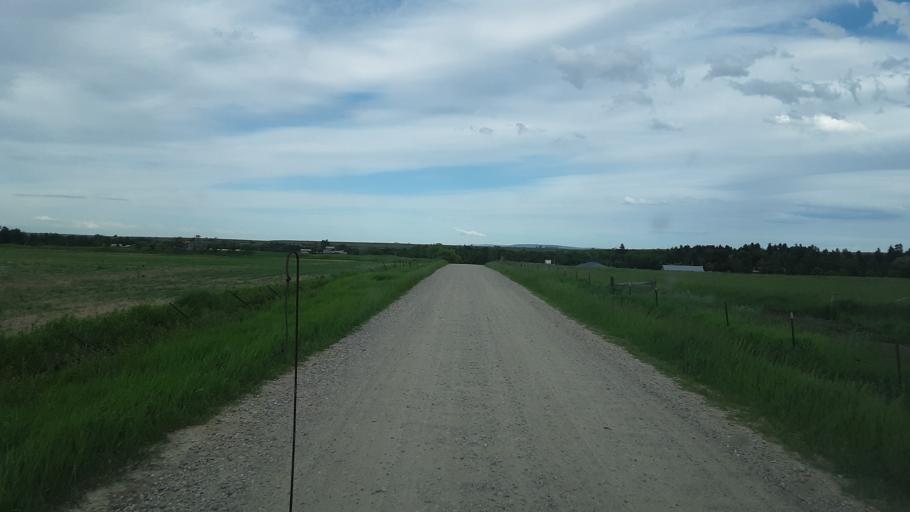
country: US
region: Montana
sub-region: Carbon County
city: Red Lodge
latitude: 45.3636
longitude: -109.1733
